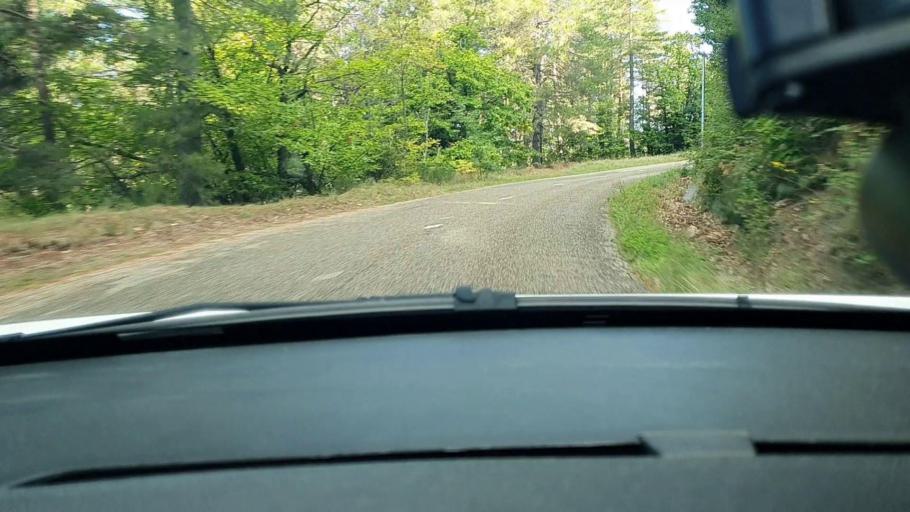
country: FR
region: Rhone-Alpes
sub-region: Departement de l'Ardeche
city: Les Vans
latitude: 44.4017
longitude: 4.0002
